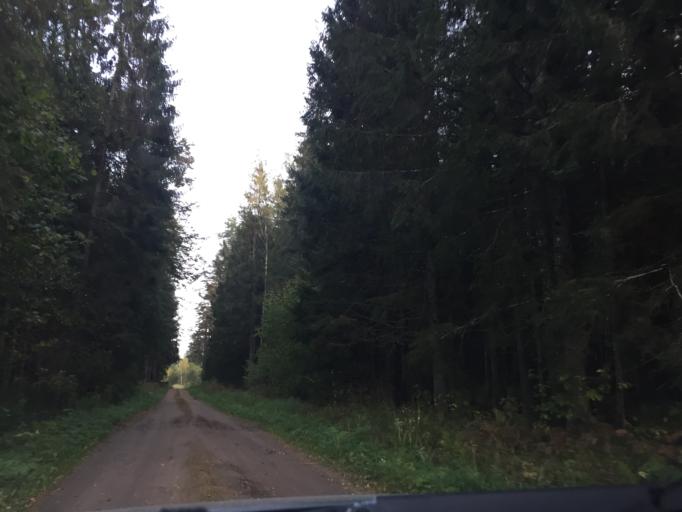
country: LV
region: Ikskile
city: Ikskile
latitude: 56.9299
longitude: 24.4911
